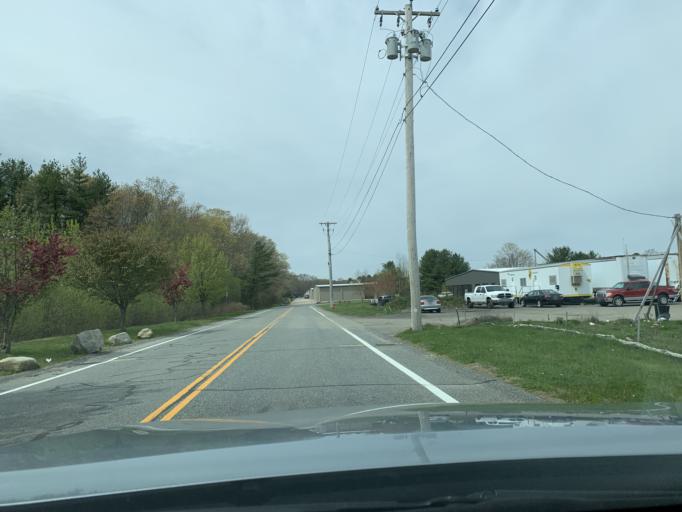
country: US
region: Rhode Island
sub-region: Washington County
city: North Kingstown
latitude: 41.6035
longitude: -71.4714
